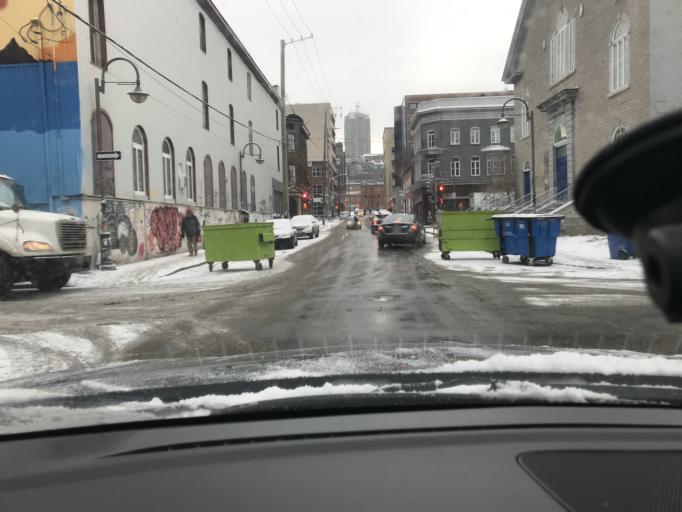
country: CA
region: Quebec
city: Quebec
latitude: 46.8127
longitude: -71.2282
